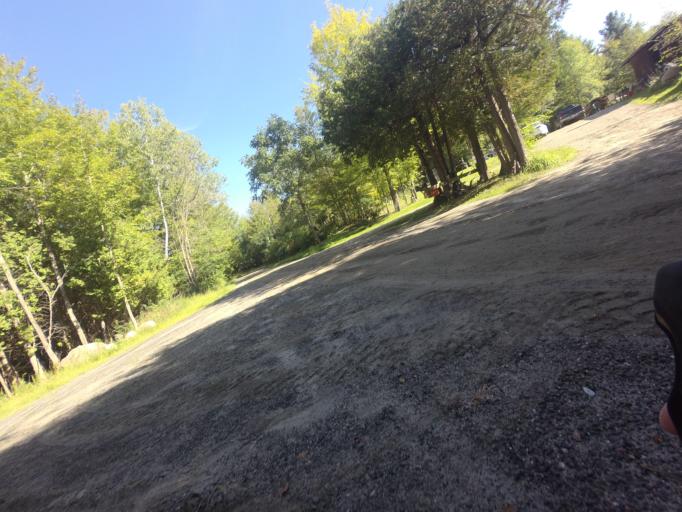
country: CA
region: Ontario
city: Perth
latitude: 44.9387
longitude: -76.3782
